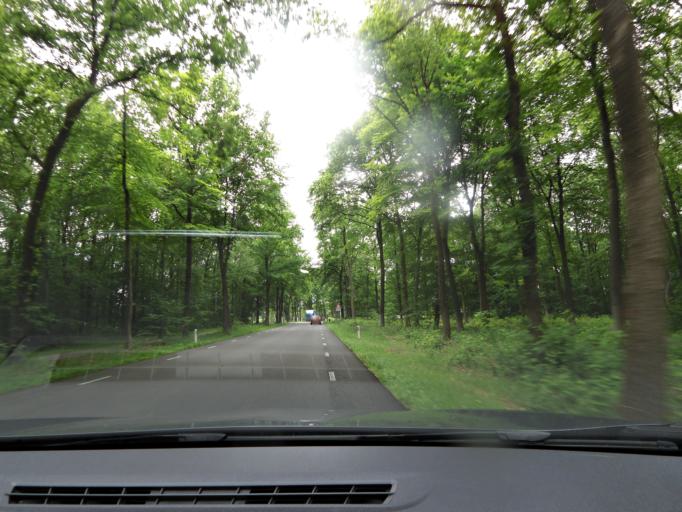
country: NL
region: Gelderland
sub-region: Gemeente Apeldoorn
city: Uddel
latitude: 52.2492
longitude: 5.7626
